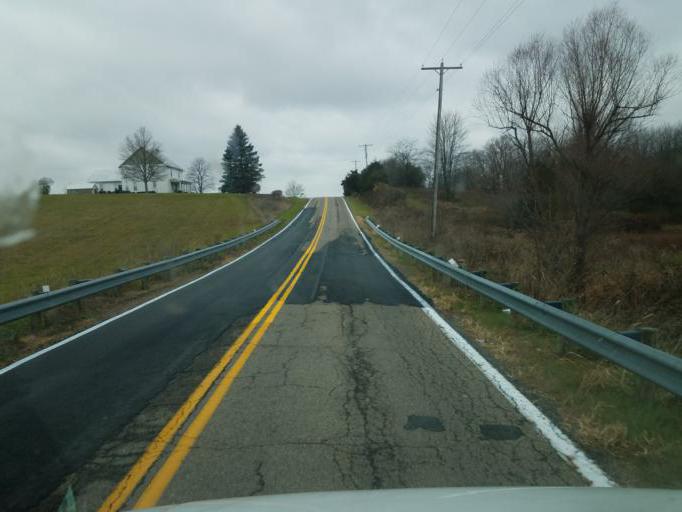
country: US
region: Ohio
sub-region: Knox County
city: Centerburg
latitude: 40.2720
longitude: -82.6305
